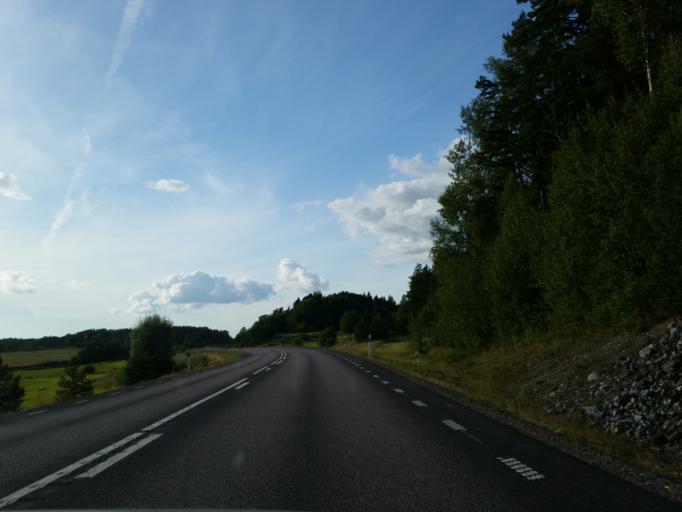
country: SE
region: Soedermanland
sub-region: Gnesta Kommun
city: Gnesta
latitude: 59.0374
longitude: 17.2991
